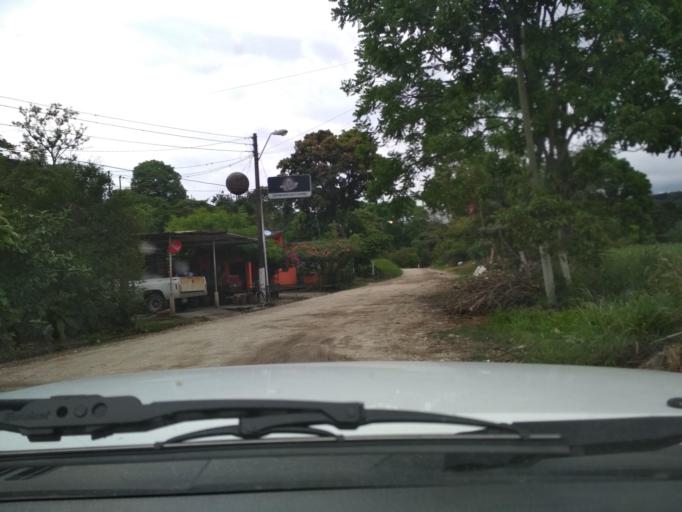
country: MX
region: Veracruz
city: Paraje Nuevo
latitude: 18.8782
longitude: -96.8828
